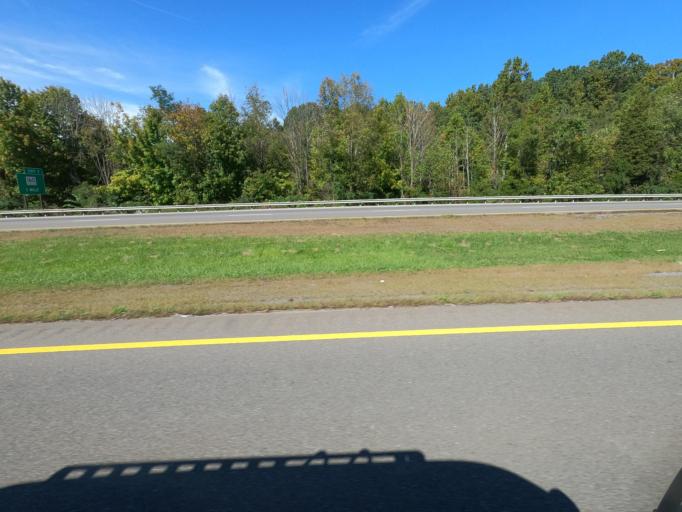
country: US
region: Tennessee
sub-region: Hamblen County
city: Morristown
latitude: 36.2082
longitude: -83.2647
